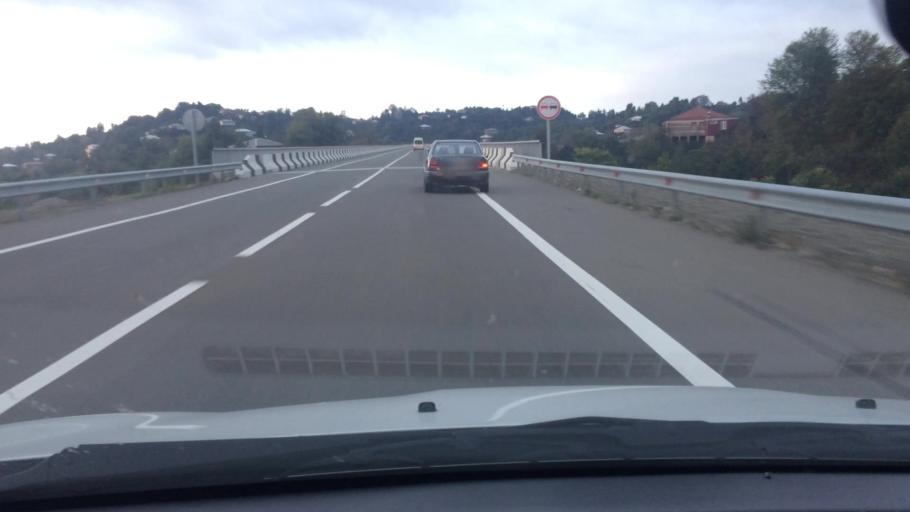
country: GE
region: Ajaria
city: Makhinjauri
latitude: 41.7299
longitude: 41.7522
